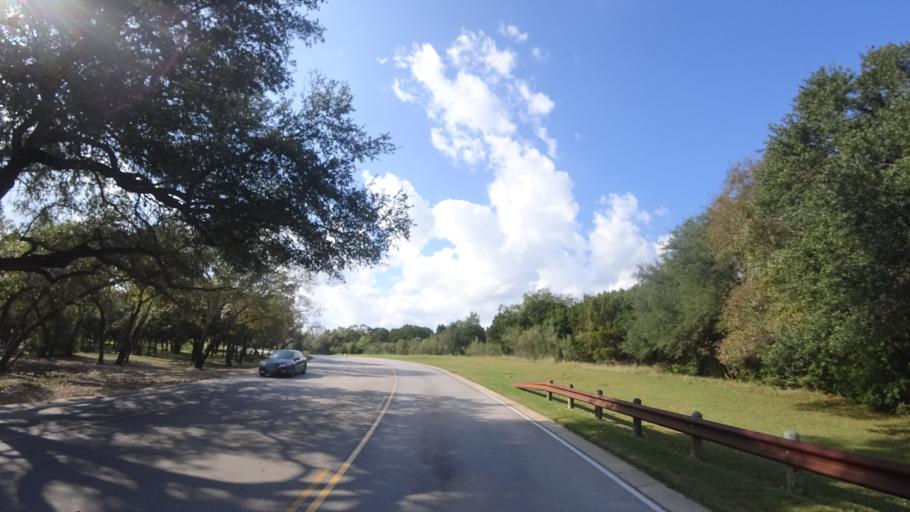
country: US
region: Texas
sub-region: Travis County
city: Lost Creek
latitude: 30.2975
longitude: -97.8553
